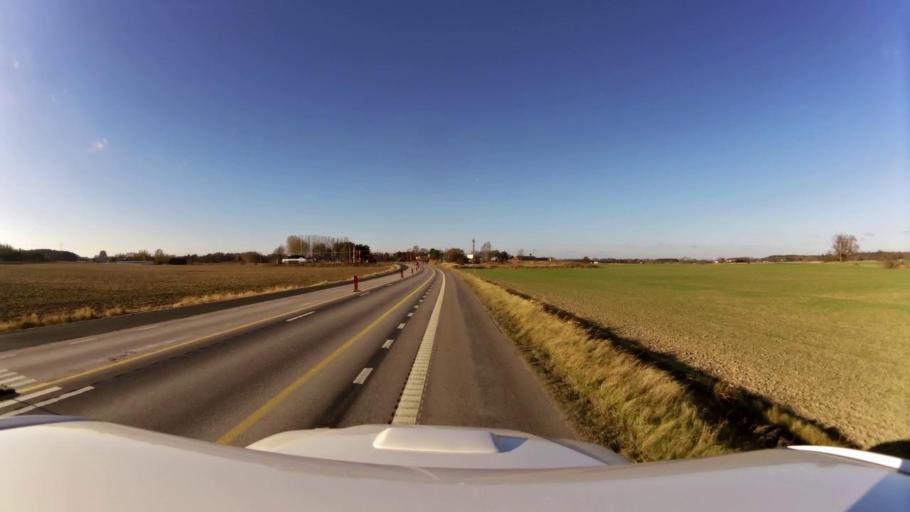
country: SE
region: OEstergoetland
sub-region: Linkopings Kommun
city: Linghem
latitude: 58.4378
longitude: 15.7565
